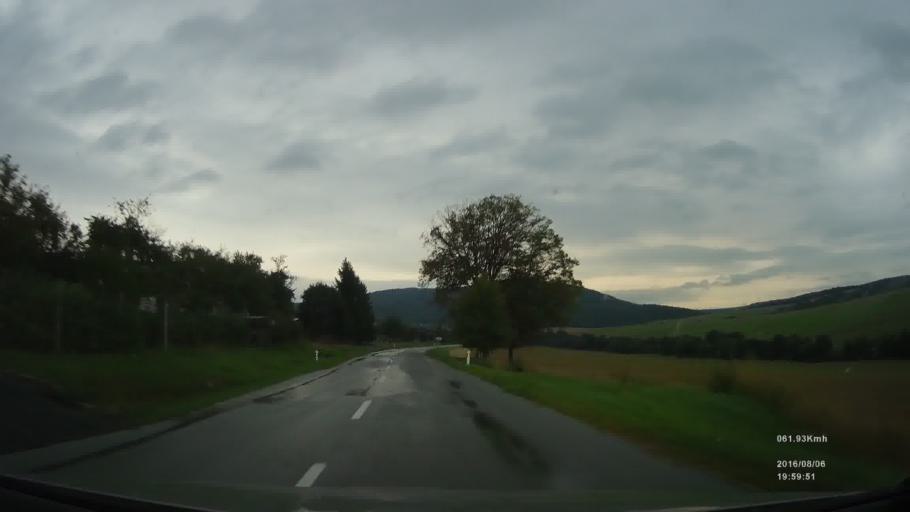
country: SK
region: Presovsky
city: Svidnik
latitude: 49.2587
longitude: 21.5804
